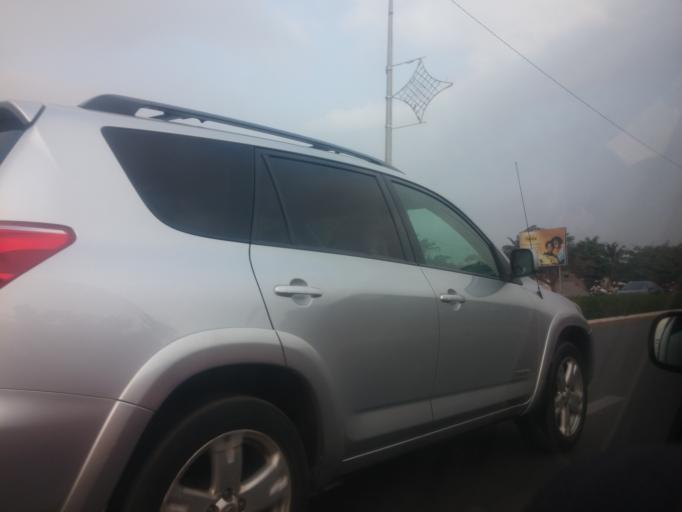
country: TG
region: Maritime
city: Lome
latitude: 6.1624
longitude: 1.2238
